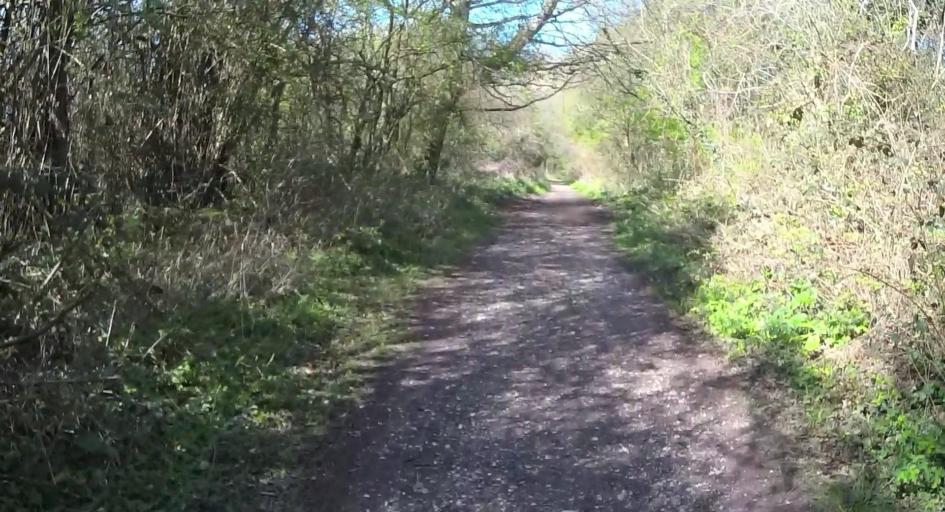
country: GB
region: England
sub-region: Hampshire
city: Abbotts Ann
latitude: 51.1025
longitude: -1.4950
